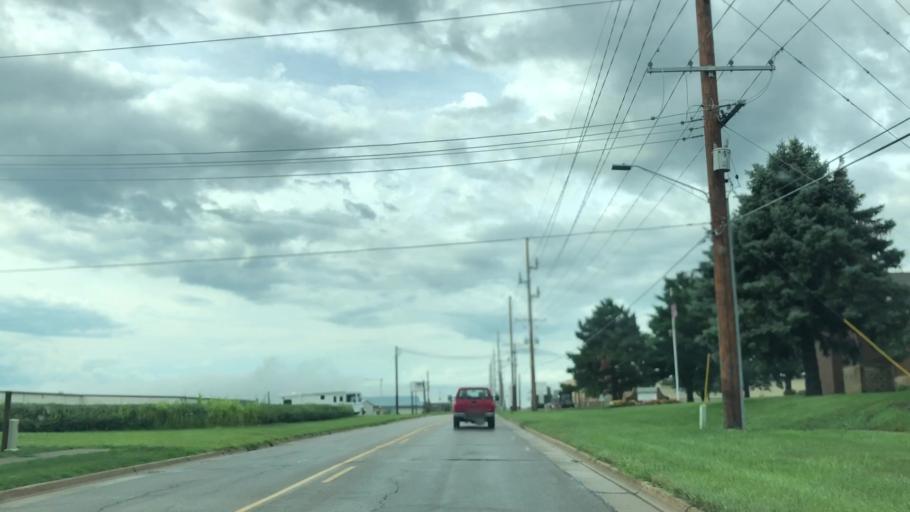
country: US
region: Iowa
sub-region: Marshall County
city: Marshalltown
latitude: 42.0106
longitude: -92.9222
